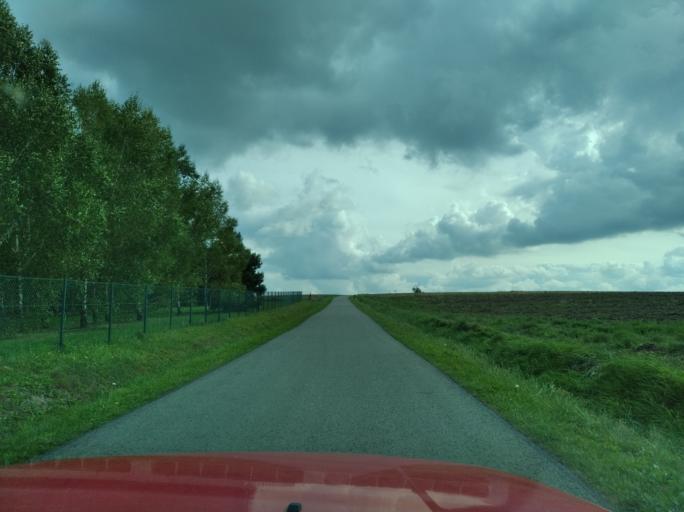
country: PL
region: Subcarpathian Voivodeship
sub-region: Powiat rzeszowski
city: Lubenia
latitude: 49.9382
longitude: 21.9404
